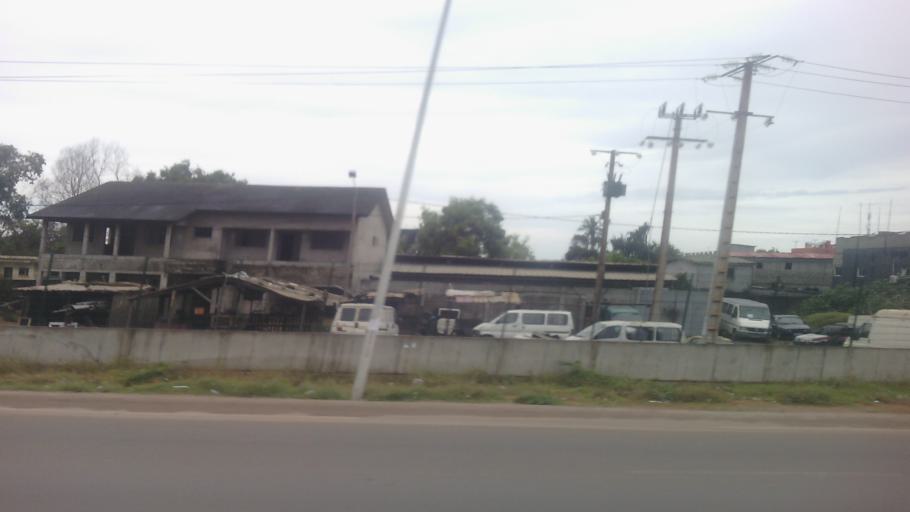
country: CI
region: Lagunes
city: Bingerville
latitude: 5.2386
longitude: -3.8915
